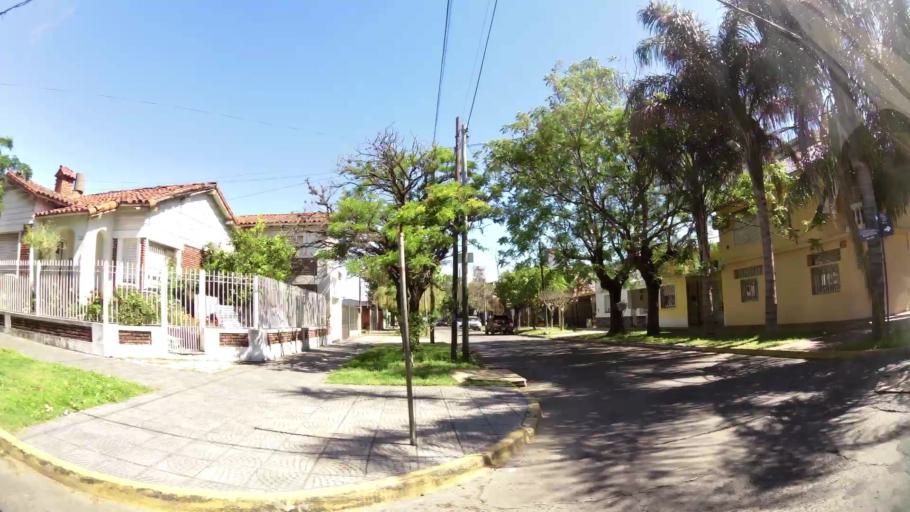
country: AR
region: Buenos Aires
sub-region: Partido de Lomas de Zamora
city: Lomas de Zamora
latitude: -34.7606
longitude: -58.4177
